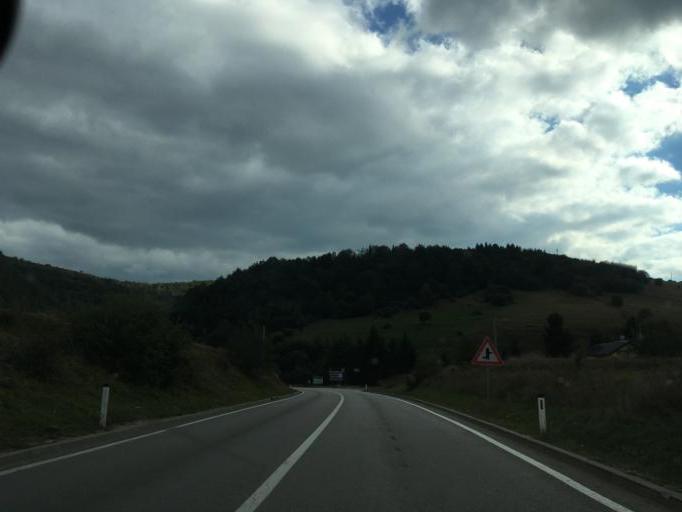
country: BA
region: Federation of Bosnia and Herzegovina
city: Novi Travnik
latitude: 44.1016
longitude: 17.5747
